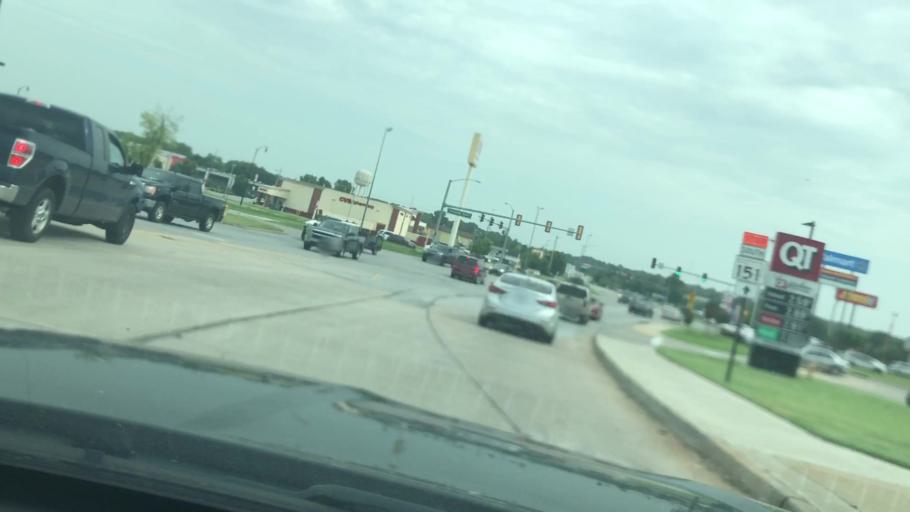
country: US
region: Oklahoma
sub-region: Tulsa County
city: Sand Springs
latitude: 36.1360
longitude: -96.1154
